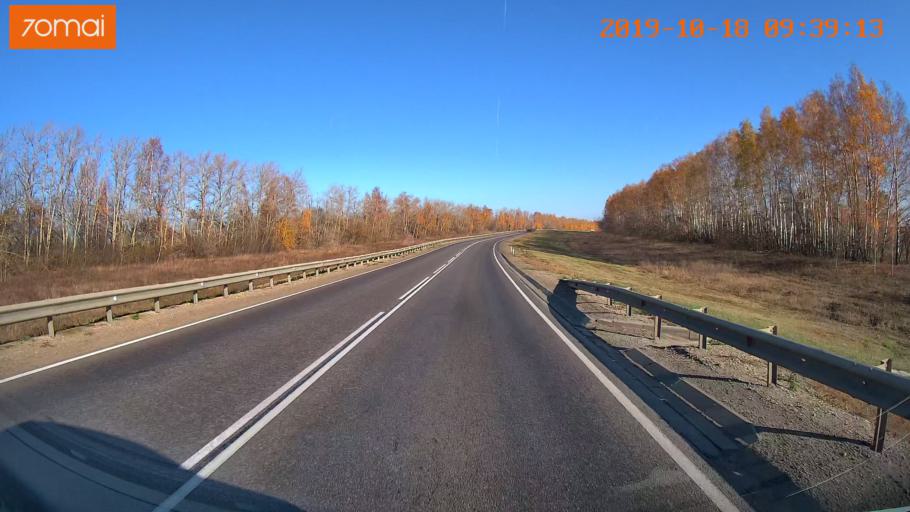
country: RU
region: Tula
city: Yefremov
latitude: 53.2501
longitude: 38.1342
